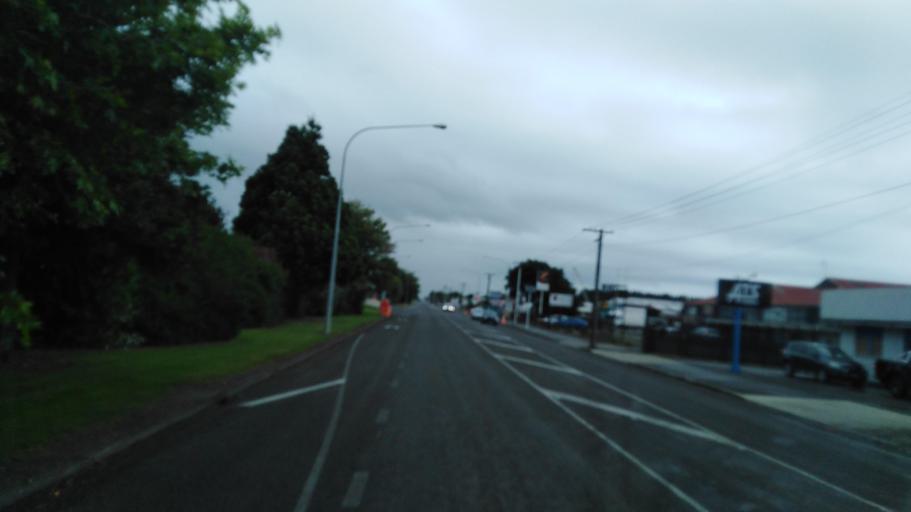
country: NZ
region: Manawatu-Wanganui
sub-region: Horowhenua District
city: Levin
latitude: -40.6353
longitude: 175.2736
